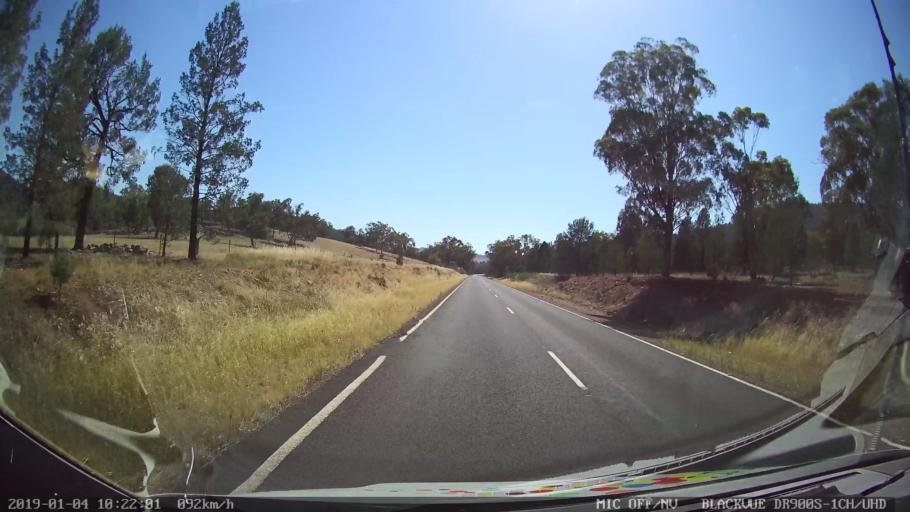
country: AU
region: New South Wales
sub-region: Cabonne
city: Canowindra
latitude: -33.3697
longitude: 148.5186
